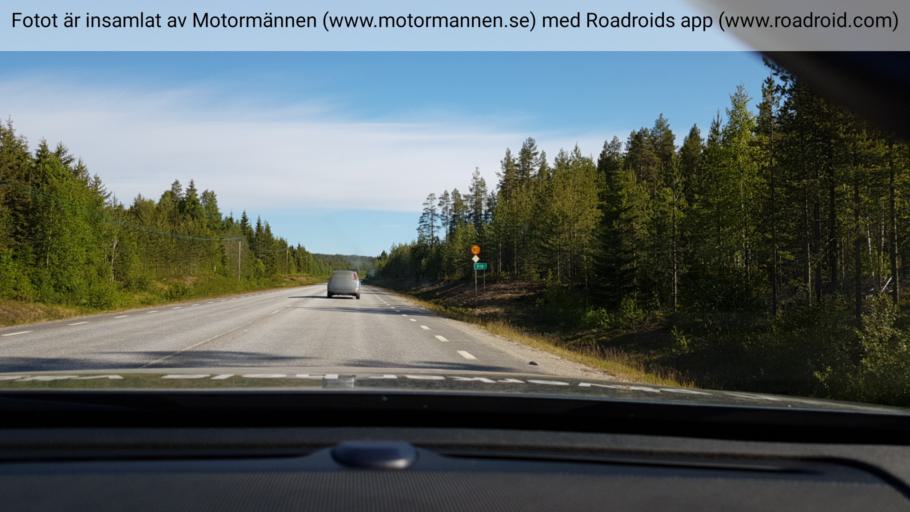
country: SE
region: Vaesterbotten
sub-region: Vannas Kommun
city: Vaennaes
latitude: 64.0142
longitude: 19.6939
